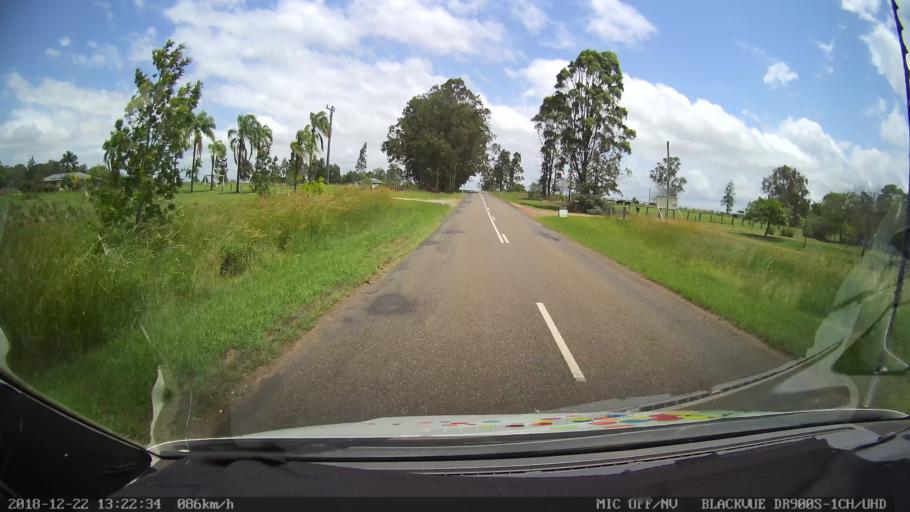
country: AU
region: New South Wales
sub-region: Clarence Valley
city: Coutts Crossing
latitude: -29.7883
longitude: 152.9109
